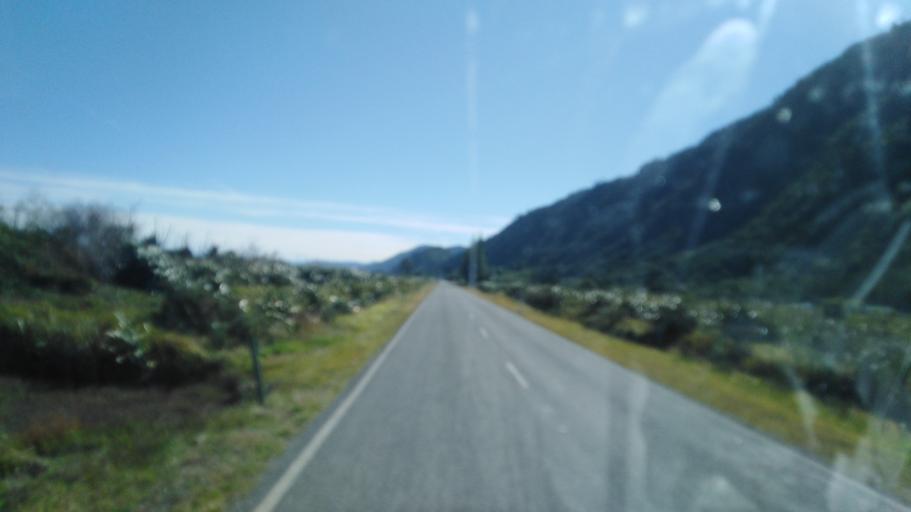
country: NZ
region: West Coast
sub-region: Buller District
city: Westport
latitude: -41.6457
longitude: 171.8374
